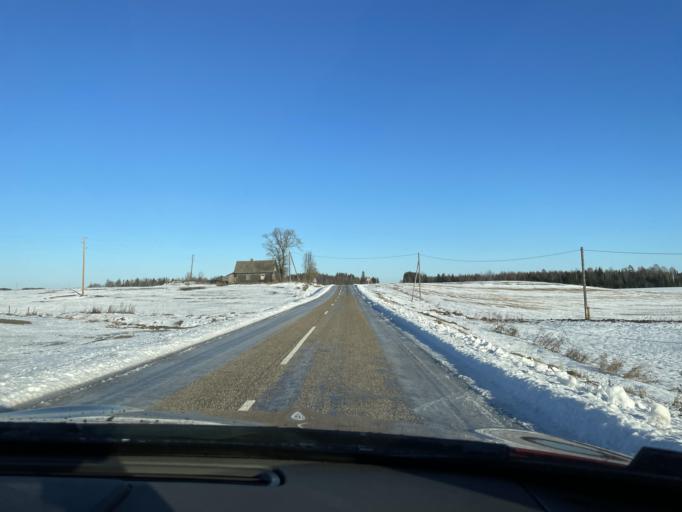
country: LV
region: Ludzas Rajons
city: Ludza
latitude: 56.4437
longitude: 27.5419
